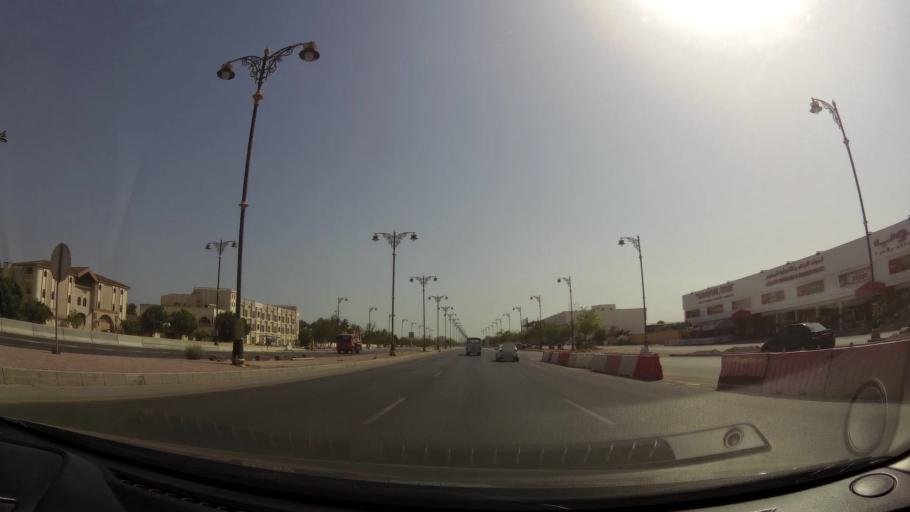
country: OM
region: Zufar
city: Salalah
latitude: 17.0151
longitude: 54.0541
